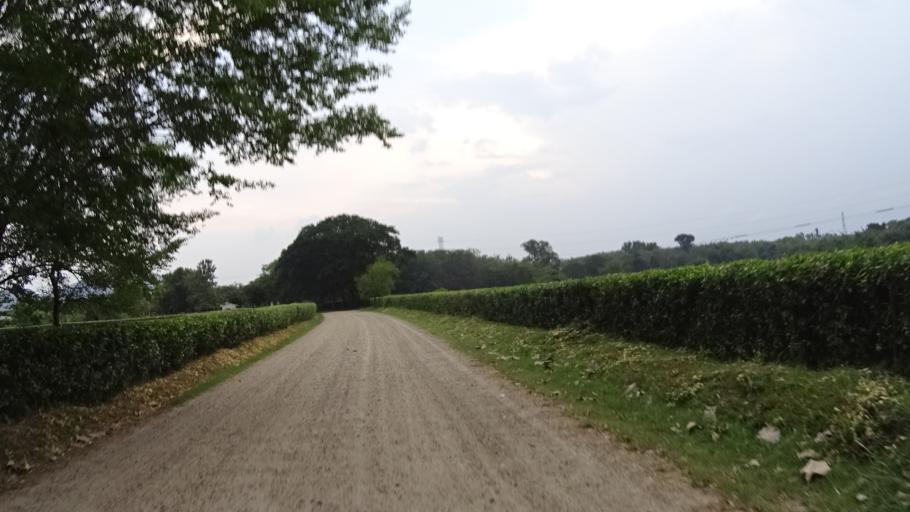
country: CO
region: Cundinamarca
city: Puerto Salgar
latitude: 5.4857
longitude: -74.6981
